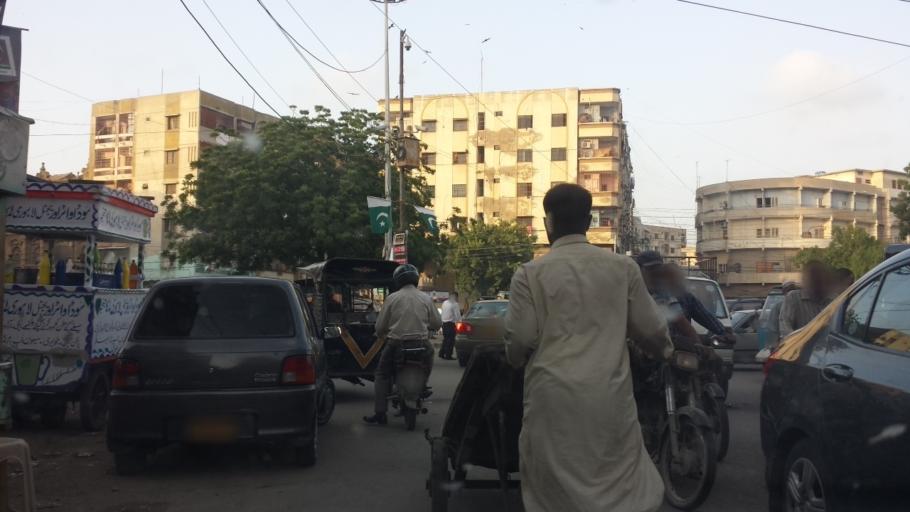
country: PK
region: Sindh
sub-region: Karachi District
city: Karachi
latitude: 24.8539
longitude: 67.0122
